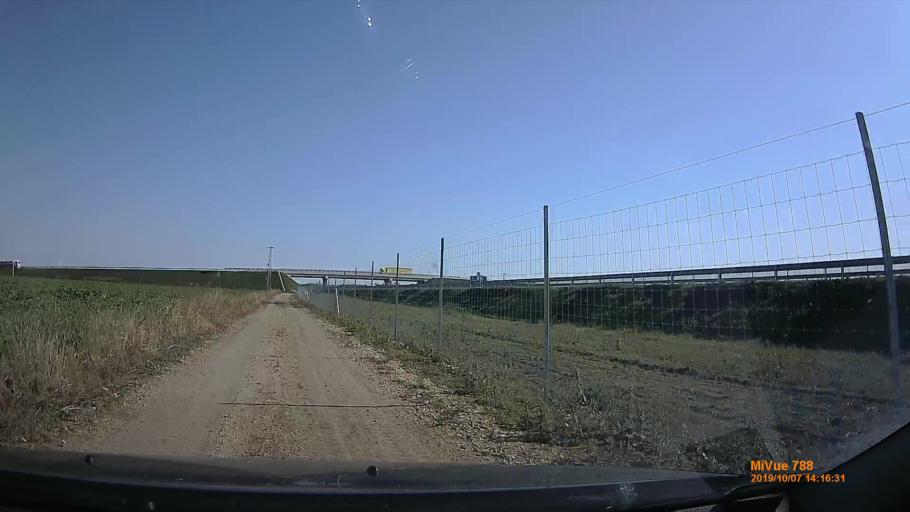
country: HU
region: Jasz-Nagykun-Szolnok
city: Kunszentmarton
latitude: 46.8736
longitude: 20.2616
